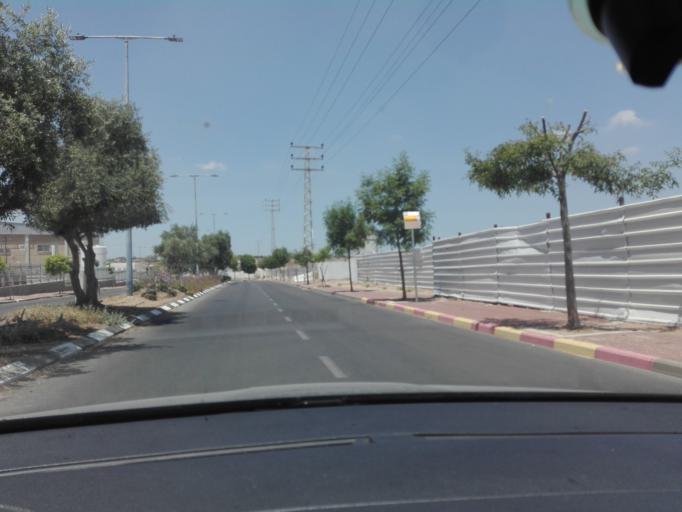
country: IL
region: Southern District
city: Qiryat Gat
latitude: 31.5950
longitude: 34.7811
